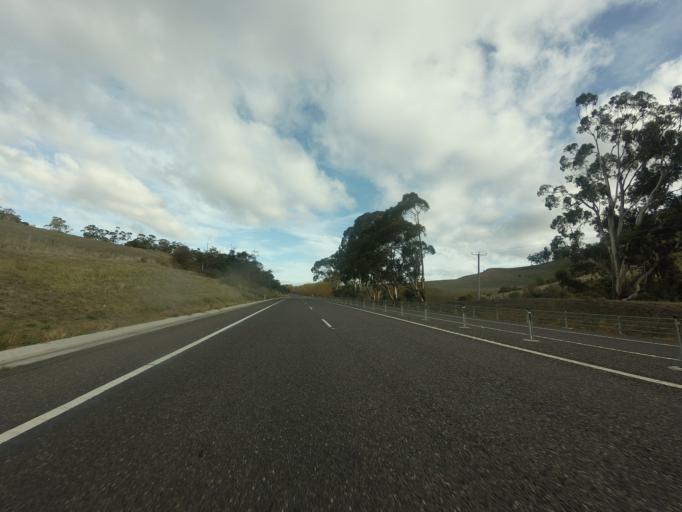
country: AU
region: Tasmania
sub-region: Brighton
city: Bridgewater
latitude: -42.5568
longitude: 147.2096
